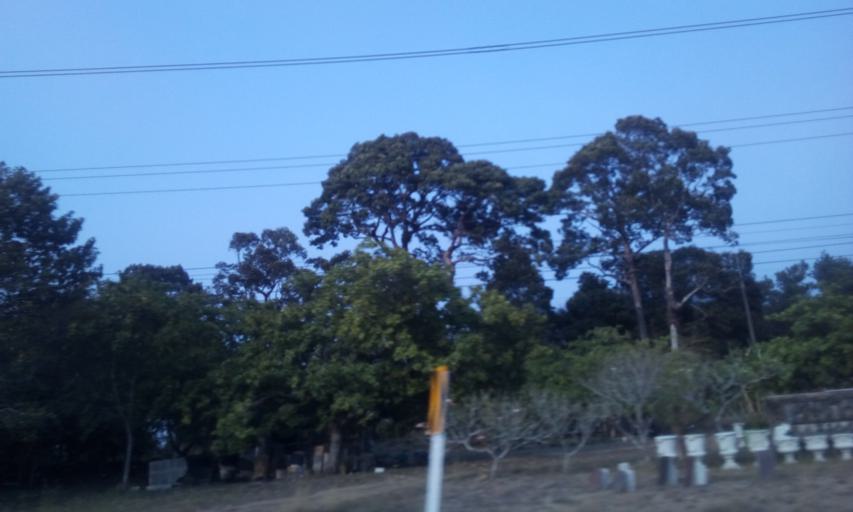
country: TH
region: Chanthaburi
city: Khlung
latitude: 12.4356
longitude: 102.3069
